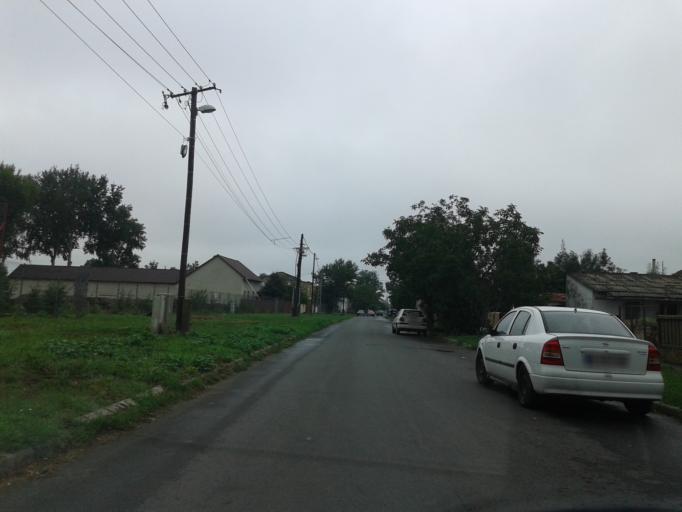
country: HU
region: Csongrad
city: Szeged
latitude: 46.2459
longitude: 20.1233
